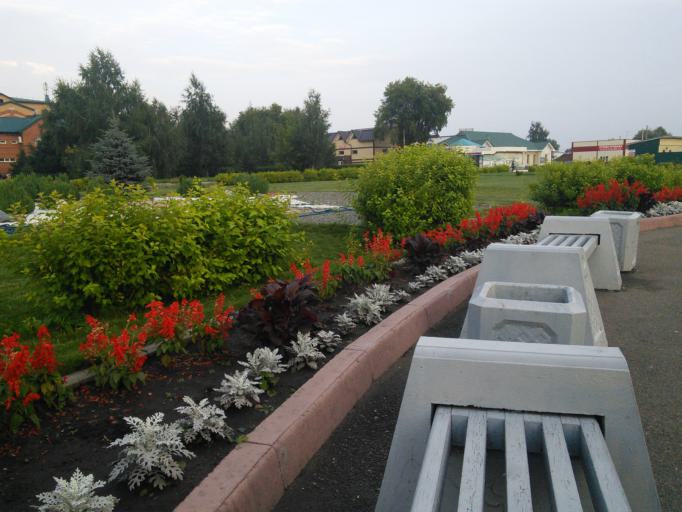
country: RU
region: Altai Krai
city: Novoaltaysk
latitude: 53.3913
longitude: 83.9319
